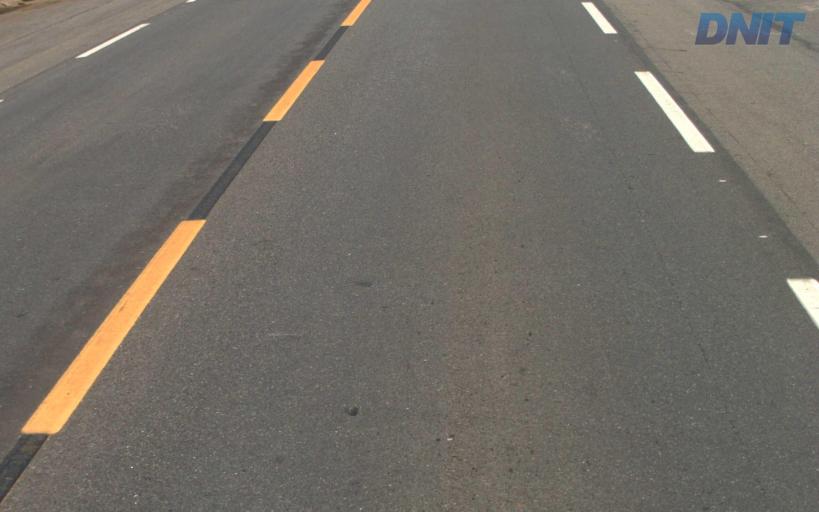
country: BR
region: Minas Gerais
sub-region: Governador Valadares
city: Governador Valadares
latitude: -18.9005
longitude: -42.0038
